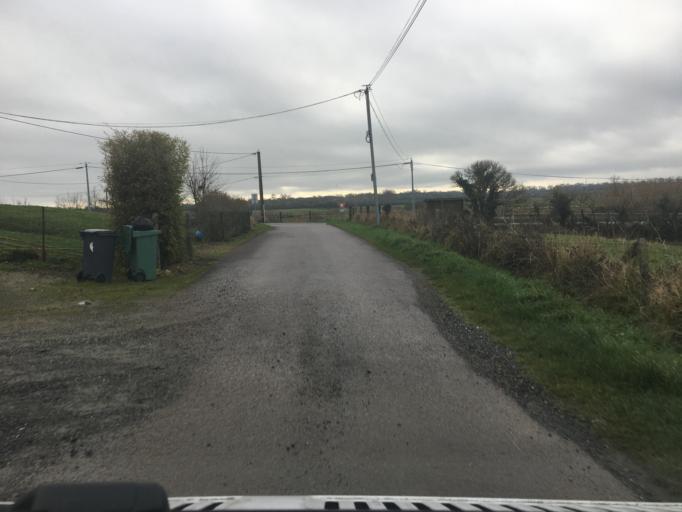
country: FR
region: Lower Normandy
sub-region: Departement du Calvados
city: Grandcamp-Maisy
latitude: 49.3901
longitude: -1.0193
